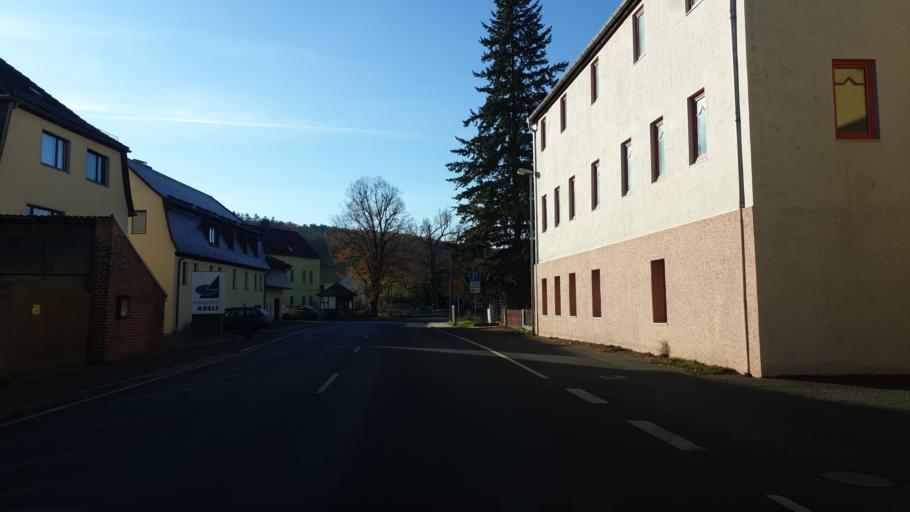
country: DE
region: Thuringia
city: Rauda
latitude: 50.9529
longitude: 11.9434
